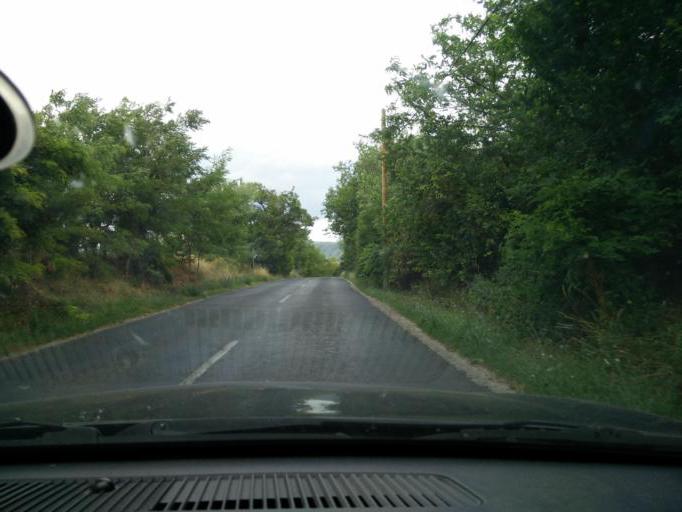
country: HU
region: Komarom-Esztergom
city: Baj
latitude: 47.6642
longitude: 18.3650
